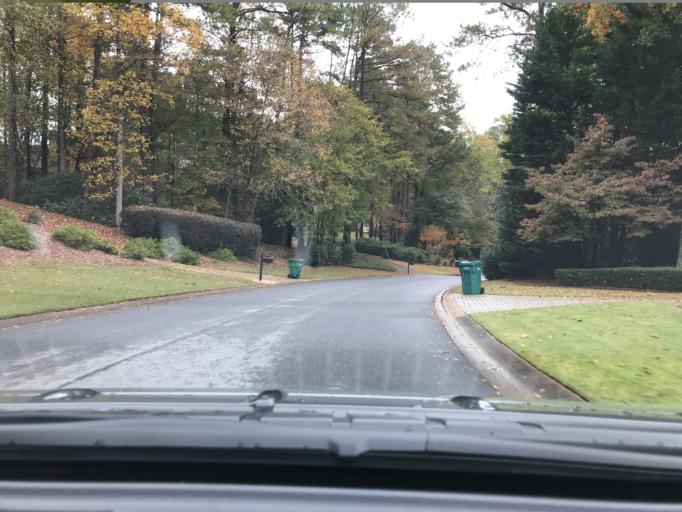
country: US
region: Georgia
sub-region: Fulton County
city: Johns Creek
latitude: 34.0058
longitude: -84.2407
